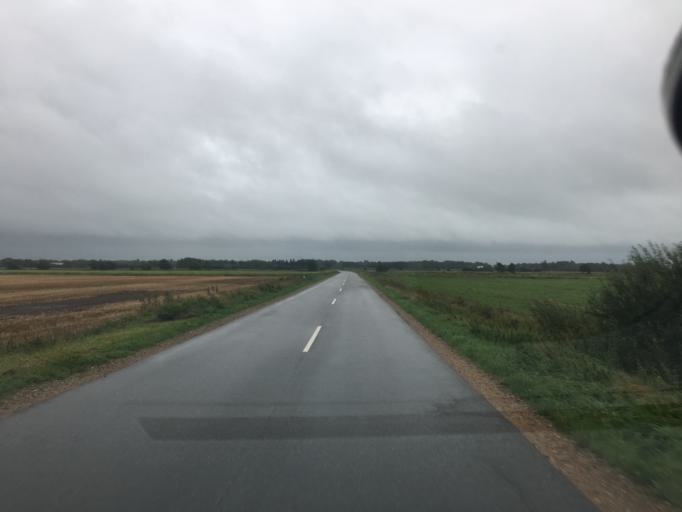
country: DE
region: Schleswig-Holstein
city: Bramstedtlund
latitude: 54.9710
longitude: 9.0445
